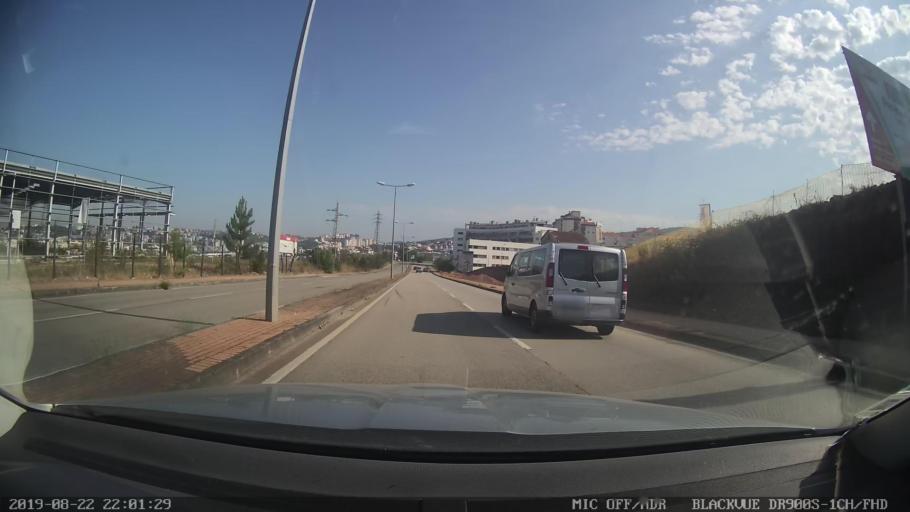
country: PT
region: Coimbra
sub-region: Coimbra
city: Coimbra
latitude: 40.1912
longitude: -8.3994
